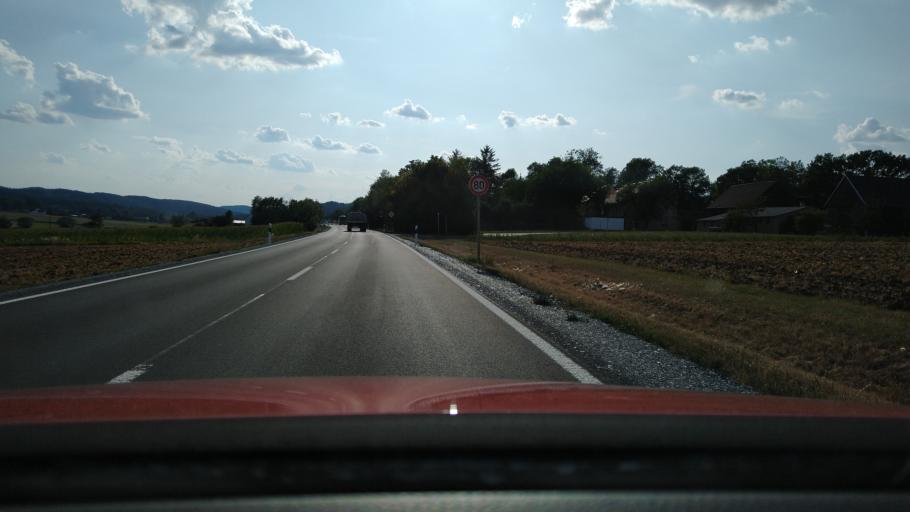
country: DE
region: Bavaria
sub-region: Upper Franconia
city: Mistelgau
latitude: 49.9294
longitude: 11.4668
